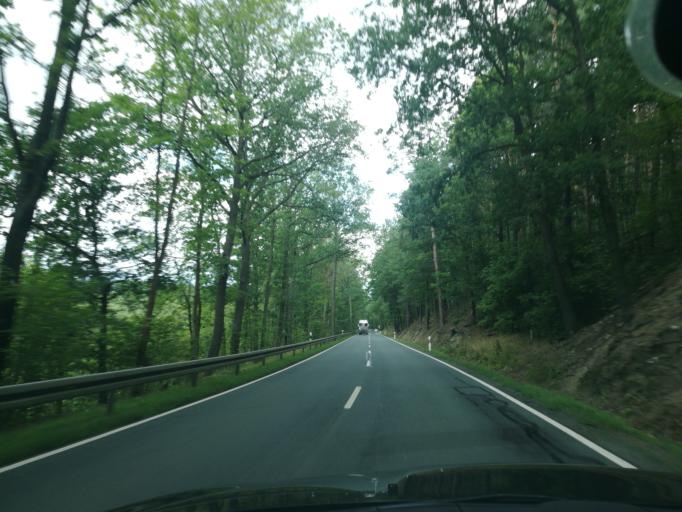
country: DE
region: Saxony
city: Oelsnitz
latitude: 50.3903
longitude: 12.1915
